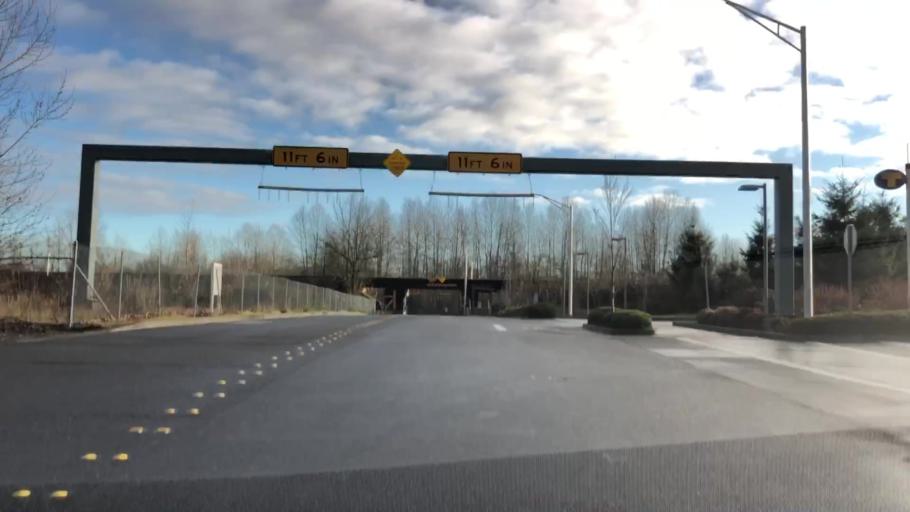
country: US
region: Washington
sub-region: King County
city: Tukwila
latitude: 47.4612
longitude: -122.2418
